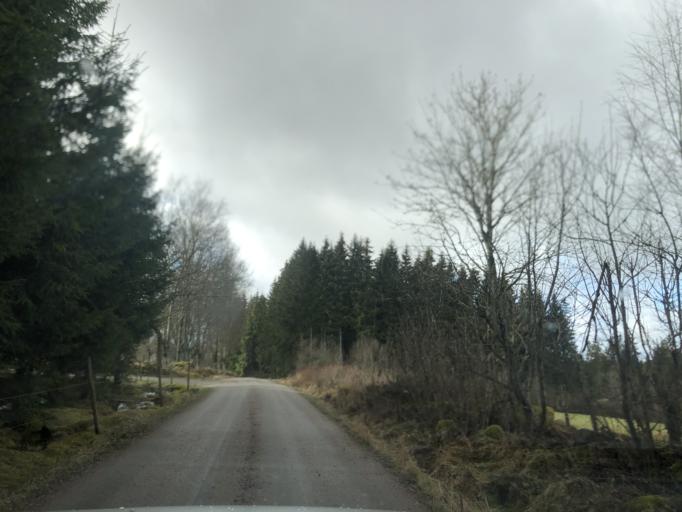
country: SE
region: Vaestra Goetaland
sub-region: Ulricehamns Kommun
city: Ulricehamn
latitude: 57.8286
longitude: 13.2418
